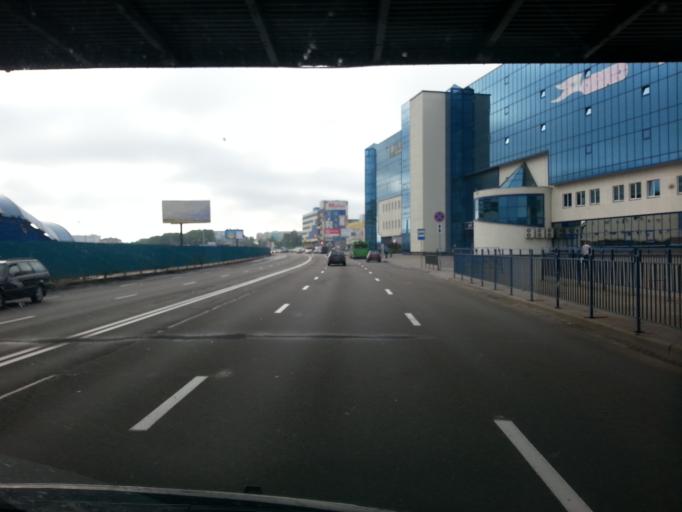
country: BY
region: Minsk
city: Zhdanovichy
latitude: 53.9336
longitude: 27.4561
